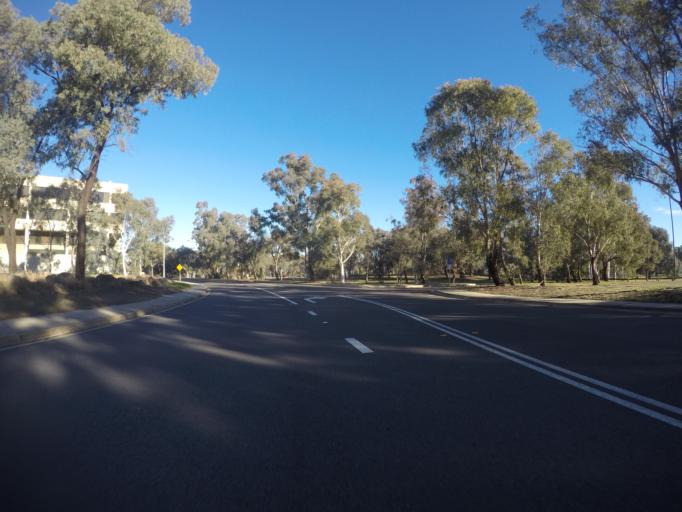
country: AU
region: Australian Capital Territory
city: Forrest
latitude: -35.3000
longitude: 149.1509
